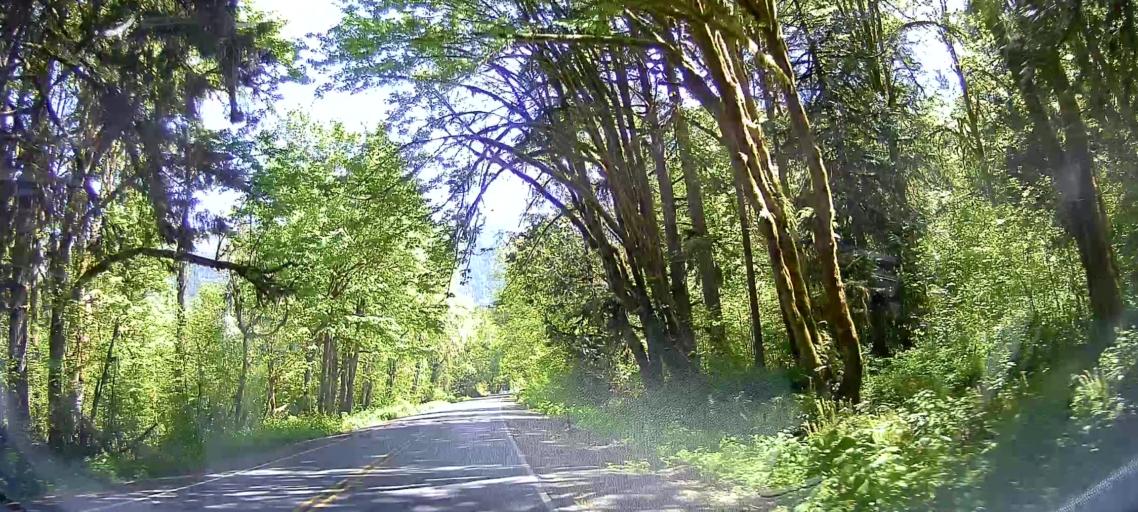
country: US
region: Washington
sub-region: Snohomish County
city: Darrington
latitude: 48.5092
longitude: -121.6845
